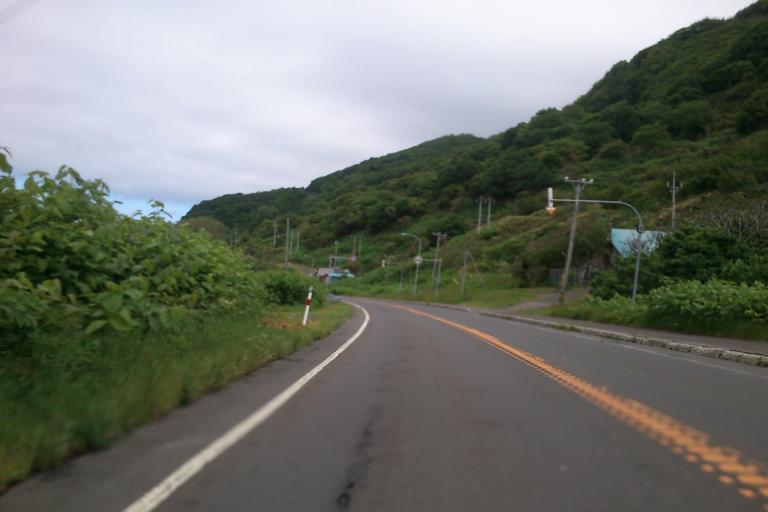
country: JP
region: Hokkaido
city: Ishikari
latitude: 43.4204
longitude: 141.4294
